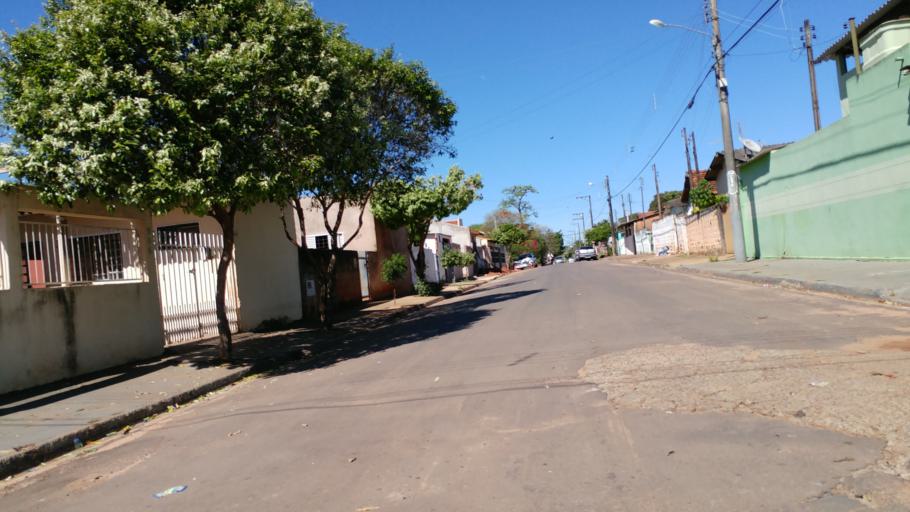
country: BR
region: Sao Paulo
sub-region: Paraguacu Paulista
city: Paraguacu Paulista
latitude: -22.4133
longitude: -50.5668
